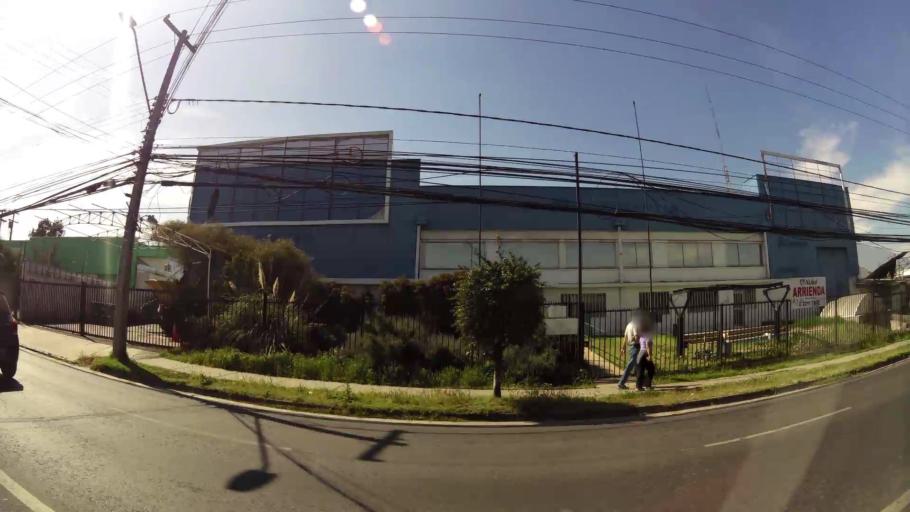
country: CL
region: Santiago Metropolitan
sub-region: Provincia de Santiago
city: Villa Presidente Frei, Nunoa, Santiago, Chile
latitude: -33.4526
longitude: -70.5439
